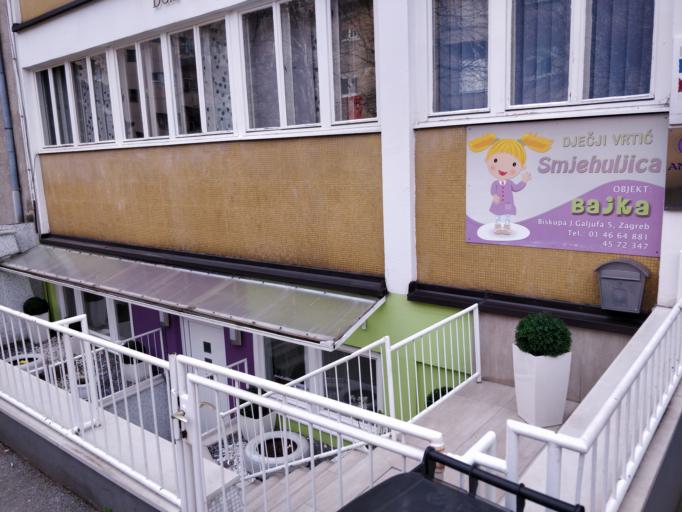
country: HR
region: Grad Zagreb
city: Zagreb
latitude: 45.8153
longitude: 15.9955
